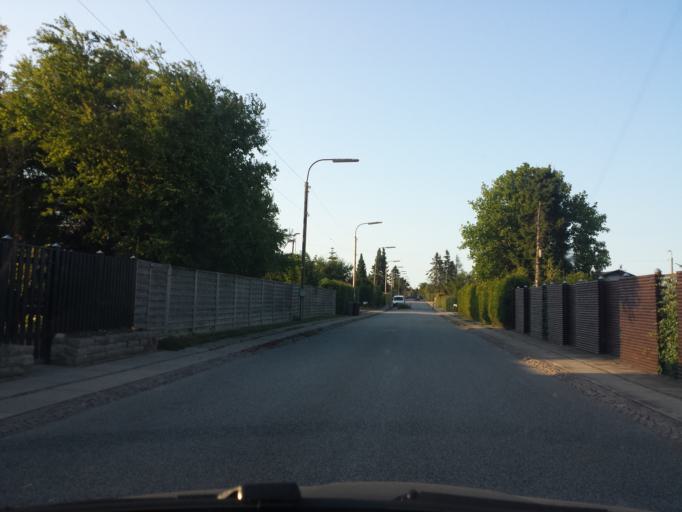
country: DK
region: Capital Region
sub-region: Ballerup Kommune
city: Ballerup
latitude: 55.7127
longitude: 12.3951
